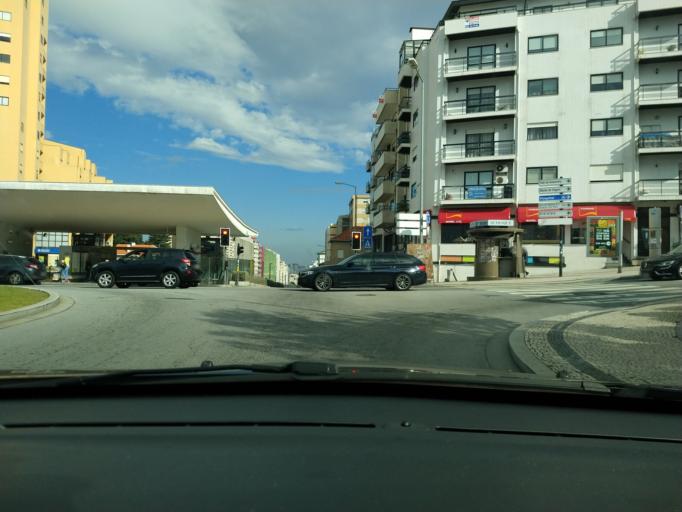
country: PT
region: Porto
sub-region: Vila Nova de Gaia
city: Vilar de Andorinho
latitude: 41.1154
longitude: -8.6064
